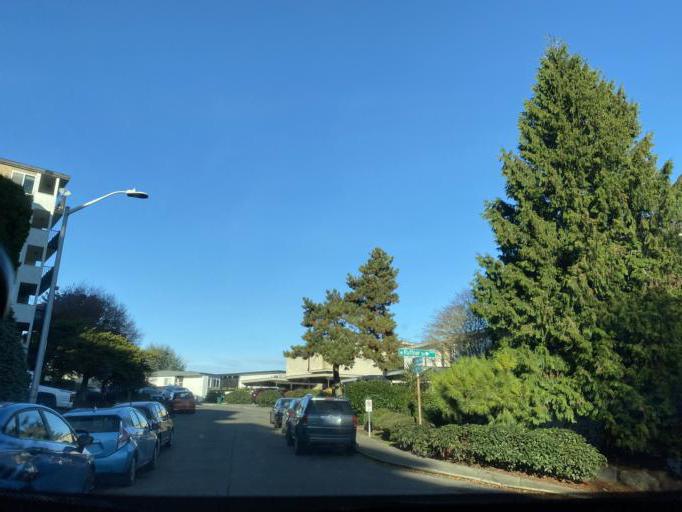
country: US
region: Washington
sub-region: King County
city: Seattle
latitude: 47.6521
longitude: -122.3888
